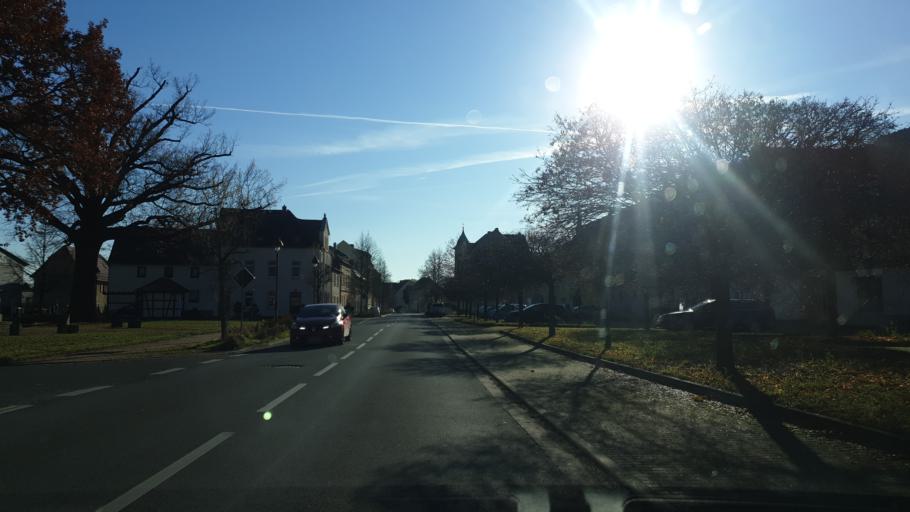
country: DE
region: Thuringia
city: Hartmannsdorf
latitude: 50.9778
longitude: 11.9790
